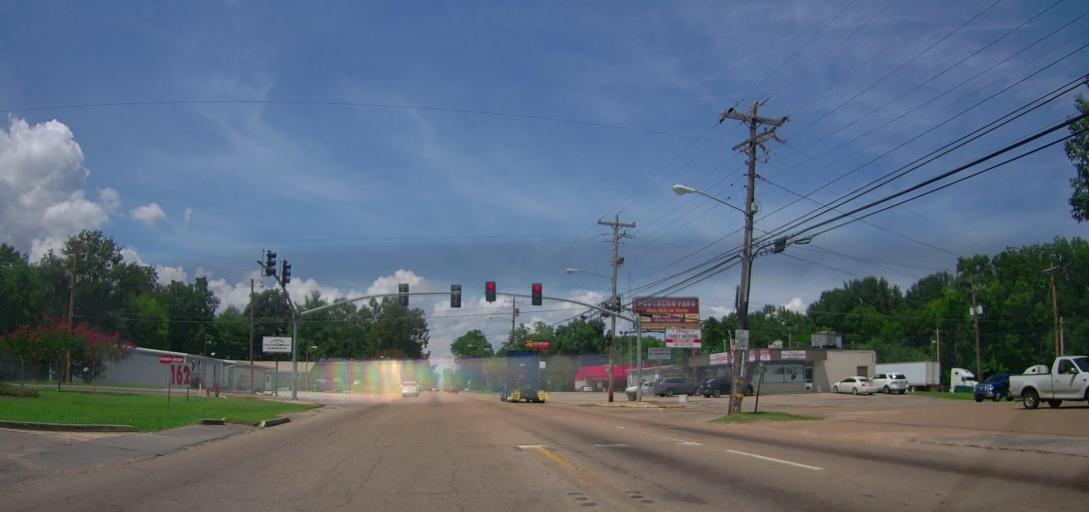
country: US
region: Mississippi
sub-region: Lee County
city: Verona
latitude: 34.1936
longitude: -88.7198
